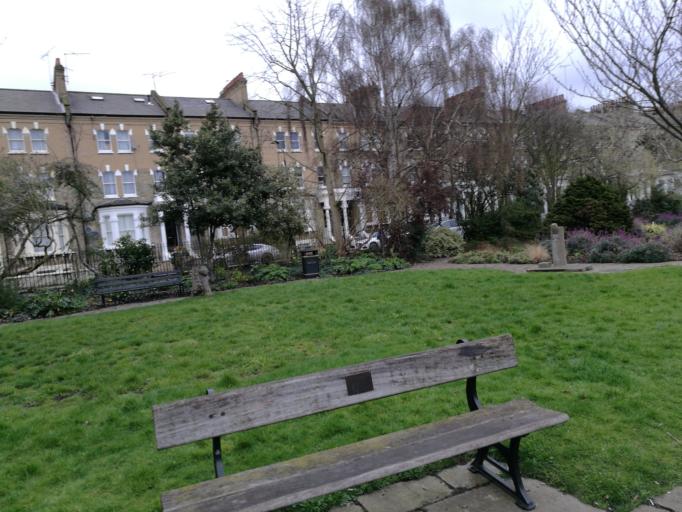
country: GB
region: England
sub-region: Greater London
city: Kensington
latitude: 51.4914
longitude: -0.2091
